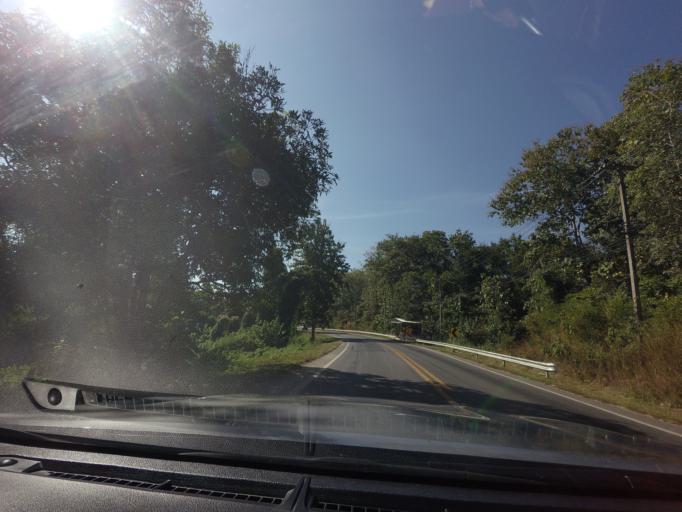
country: TH
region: Sukhothai
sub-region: Amphoe Si Satchanalai
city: Si Satchanalai
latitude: 17.6321
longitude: 99.6908
